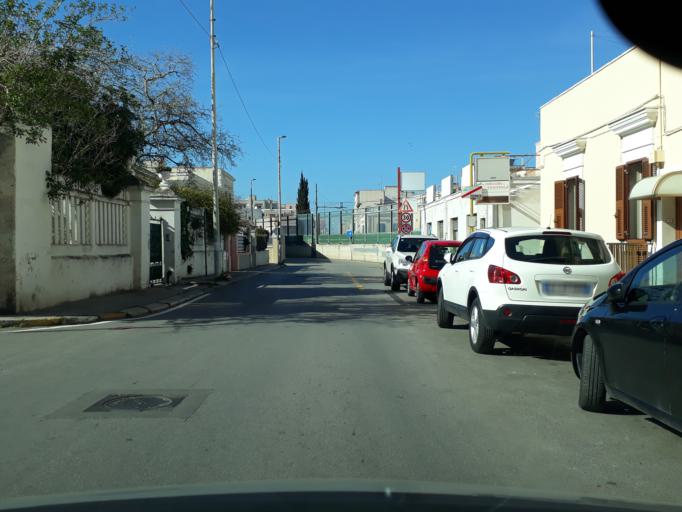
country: IT
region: Apulia
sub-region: Provincia di Bari
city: Monopoli
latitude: 40.9480
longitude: 17.2990
